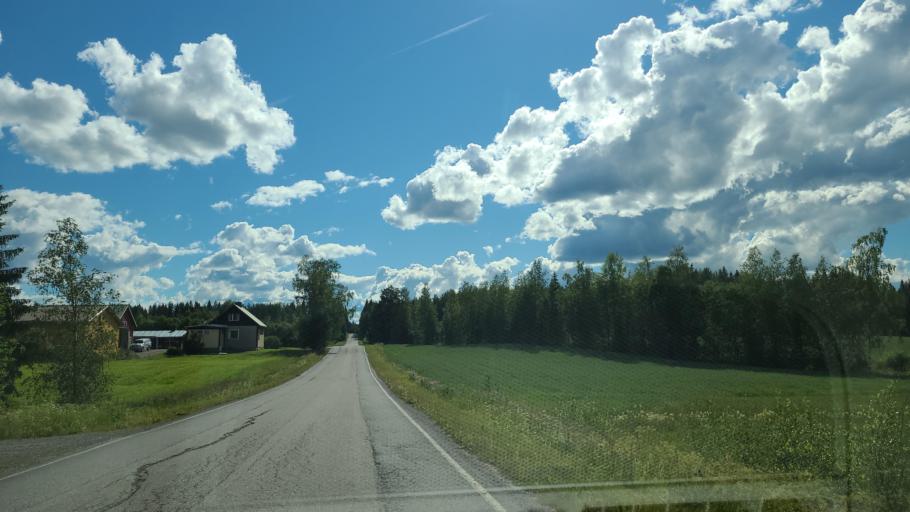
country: FI
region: Central Finland
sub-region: Jaemsae
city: Jaemsae
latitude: 61.8840
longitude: 25.2350
